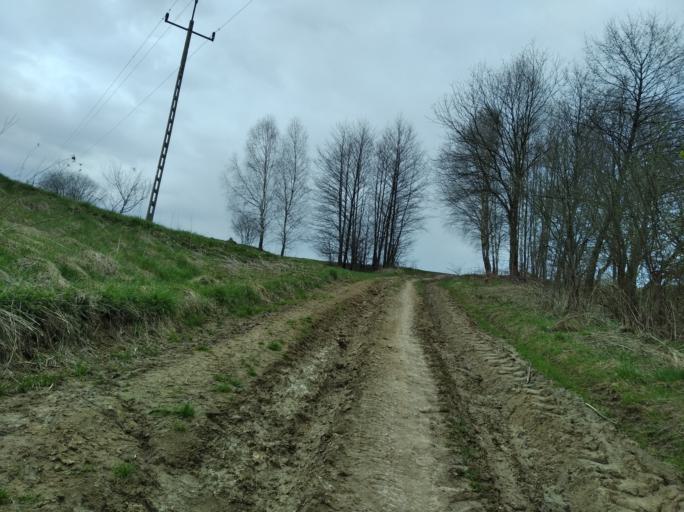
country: PL
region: Subcarpathian Voivodeship
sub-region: Powiat strzyzowski
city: Strzyzow
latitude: 49.8489
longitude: 21.7866
